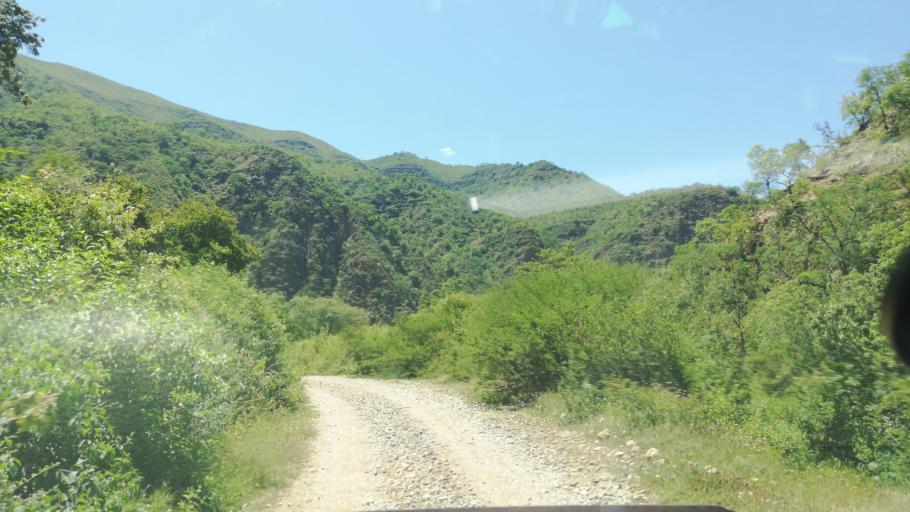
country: BO
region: Cochabamba
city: Mizque
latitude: -17.8271
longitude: -65.2947
